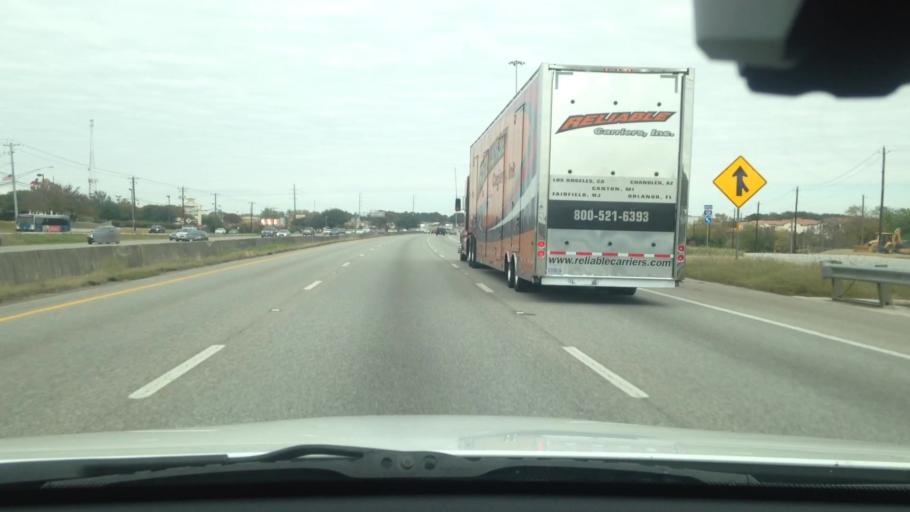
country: US
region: Texas
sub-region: Travis County
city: Onion Creek
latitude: 30.1609
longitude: -97.7889
